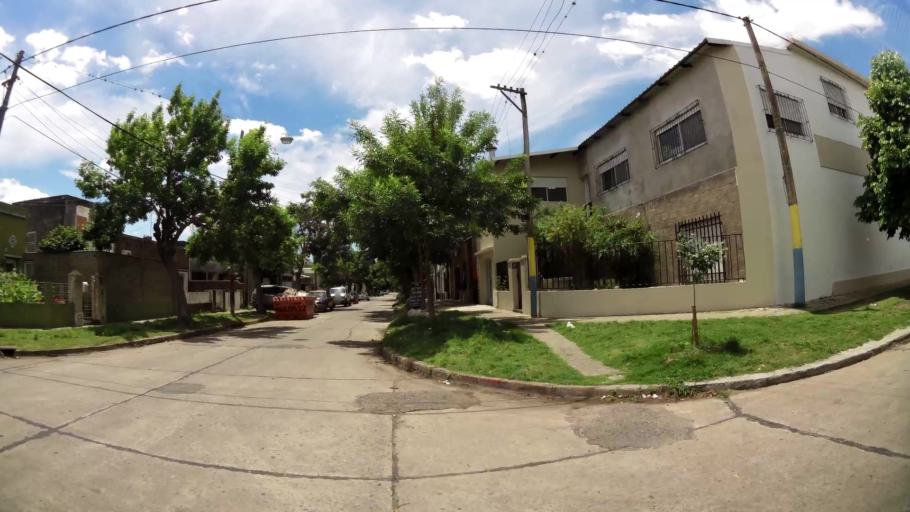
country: AR
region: Santa Fe
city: Gobernador Galvez
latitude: -33.0010
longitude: -60.6230
